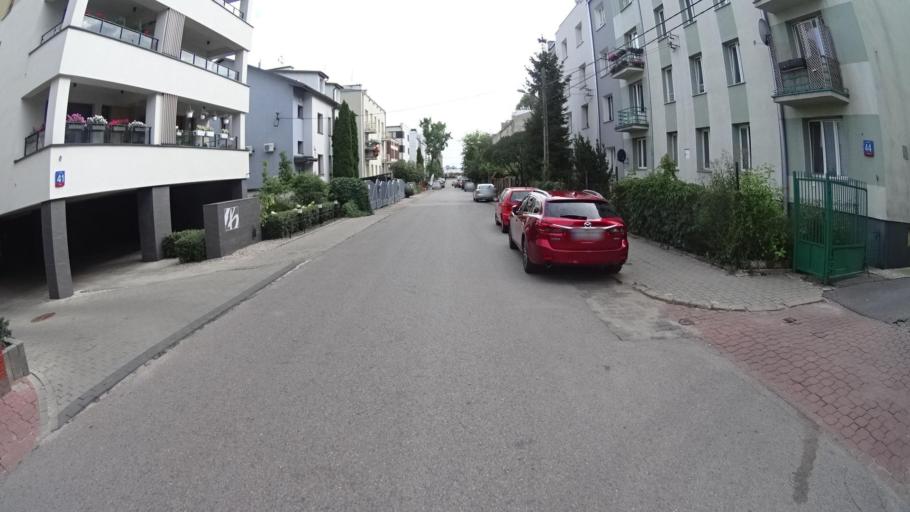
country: PL
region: Masovian Voivodeship
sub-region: Warszawa
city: Wlochy
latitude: 52.1874
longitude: 20.9578
